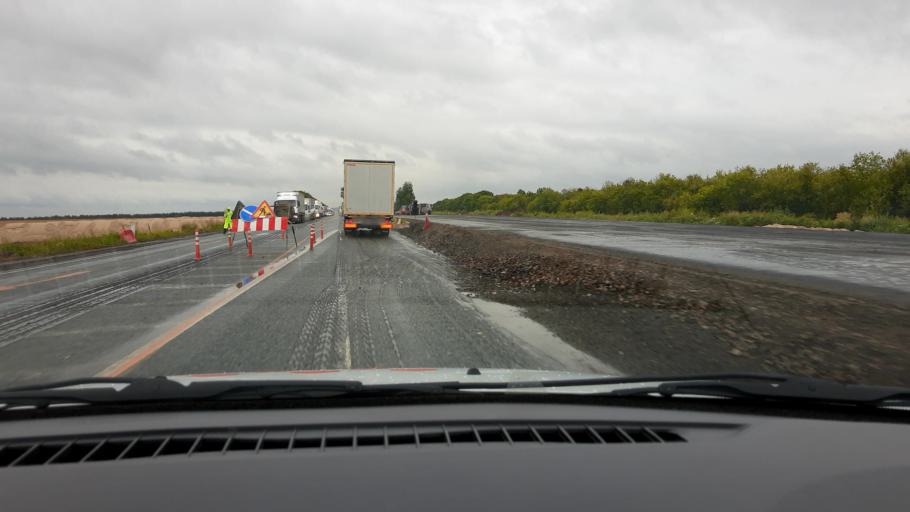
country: RU
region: Chuvashia
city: Yantikovo
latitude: 55.8026
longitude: 47.8958
